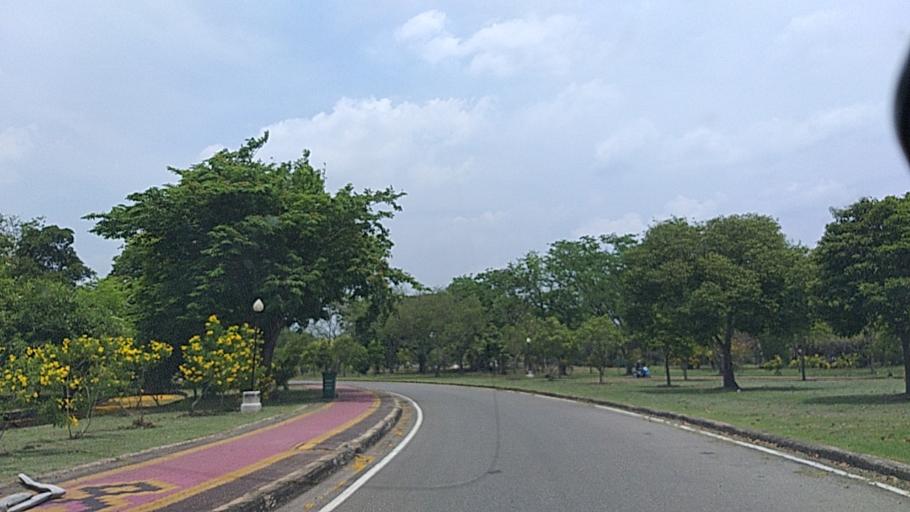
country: TH
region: Bangkok
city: Thawi Watthana
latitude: 13.7727
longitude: 100.3254
